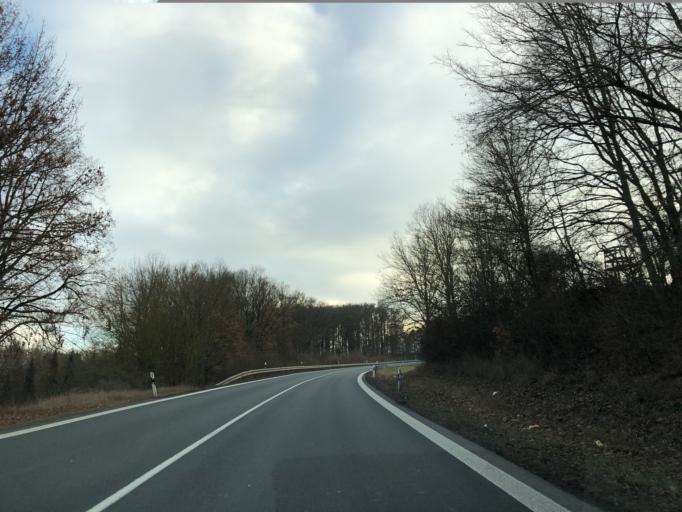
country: DE
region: Bavaria
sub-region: Regierungsbezirk Unterfranken
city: Waldbrunn
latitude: 49.7718
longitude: 9.7746
